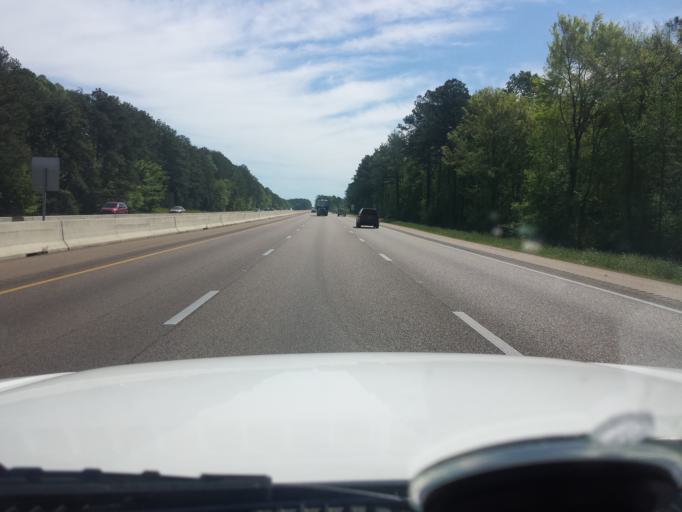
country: US
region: Mississippi
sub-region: Rankin County
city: Pearl
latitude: 32.2664
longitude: -90.1233
